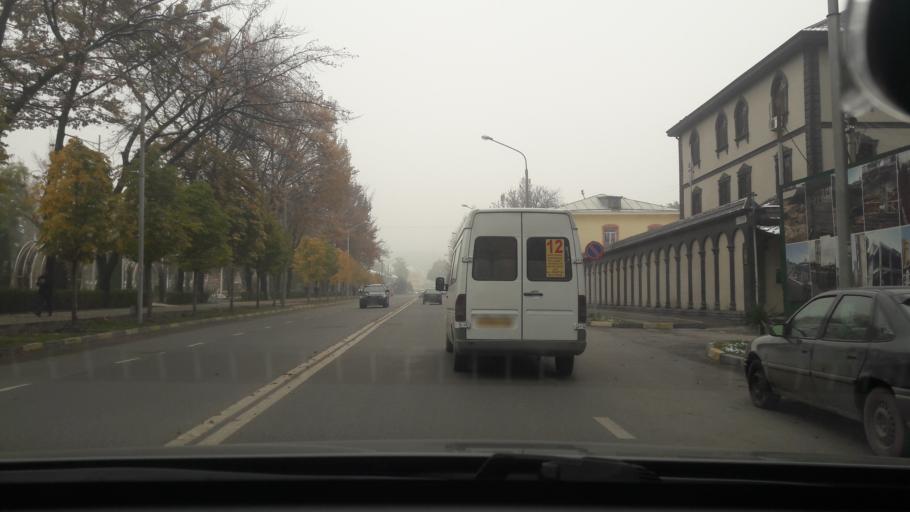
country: TJ
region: Dushanbe
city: Dushanbe
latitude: 38.5788
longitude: 68.7951
